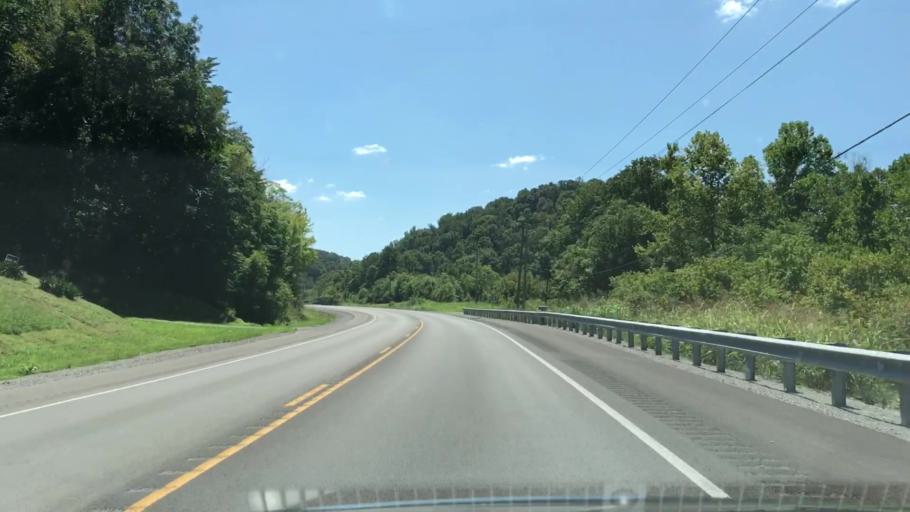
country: US
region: Kentucky
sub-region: Cumberland County
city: Burkesville
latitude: 36.7271
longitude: -85.3717
